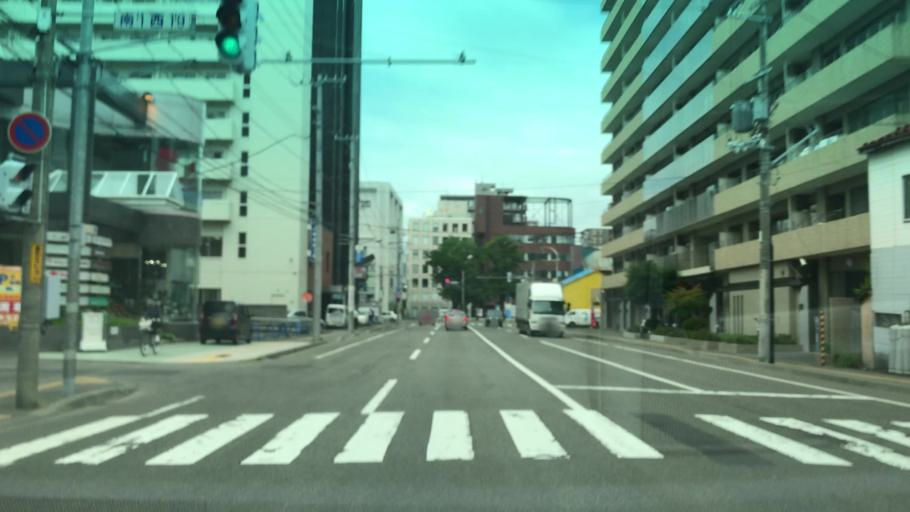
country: JP
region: Hokkaido
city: Sapporo
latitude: 43.0558
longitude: 141.3290
